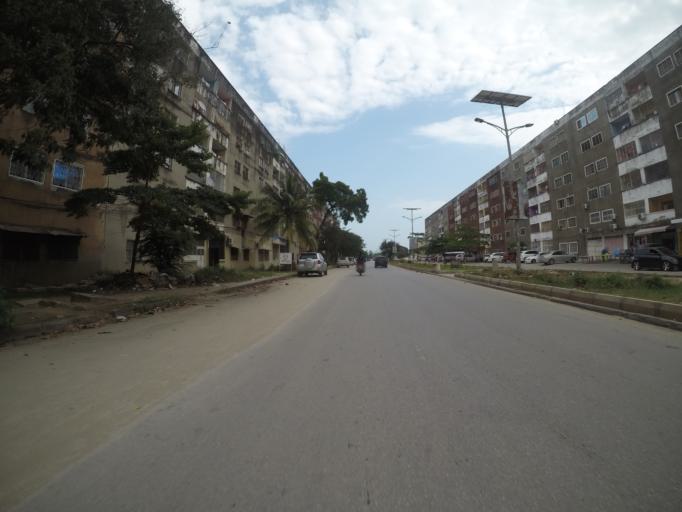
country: TZ
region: Zanzibar Urban/West
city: Zanzibar
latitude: -6.1690
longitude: 39.1988
